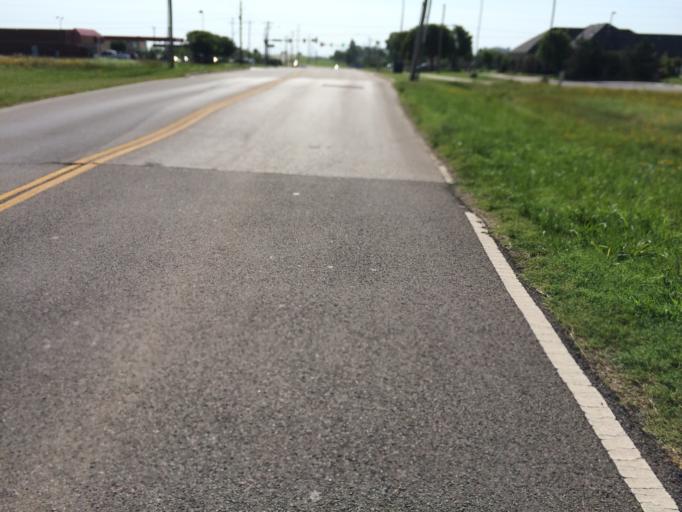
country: US
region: Oklahoma
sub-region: Cleveland County
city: Norman
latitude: 35.2474
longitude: -97.4963
